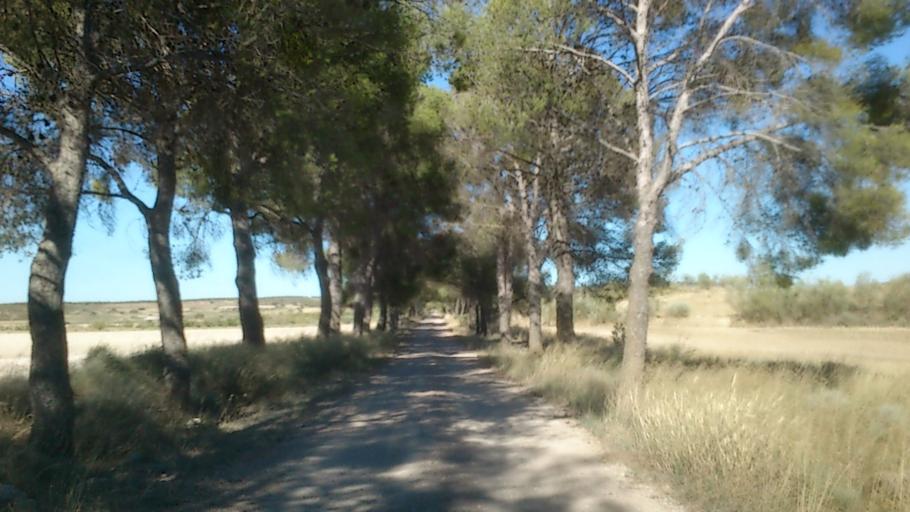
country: ES
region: Aragon
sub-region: Provincia de Zaragoza
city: San Mateo de Gallego
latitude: 41.7690
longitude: -0.7390
